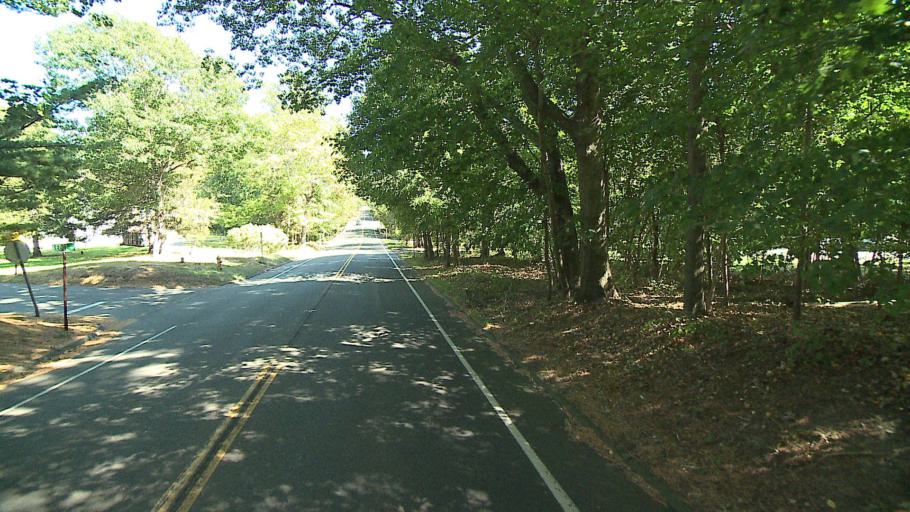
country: US
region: Connecticut
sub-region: New Haven County
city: Woodbridge
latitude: 41.3528
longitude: -73.0227
